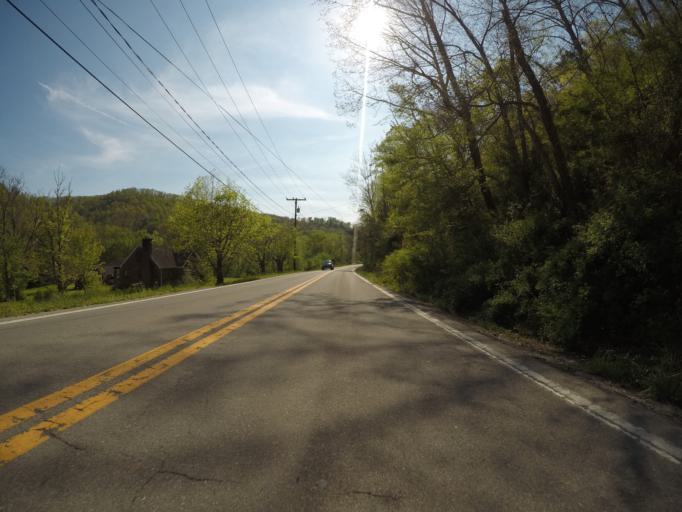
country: US
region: West Virginia
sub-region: Kanawha County
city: Elkview
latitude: 38.4607
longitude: -81.4151
